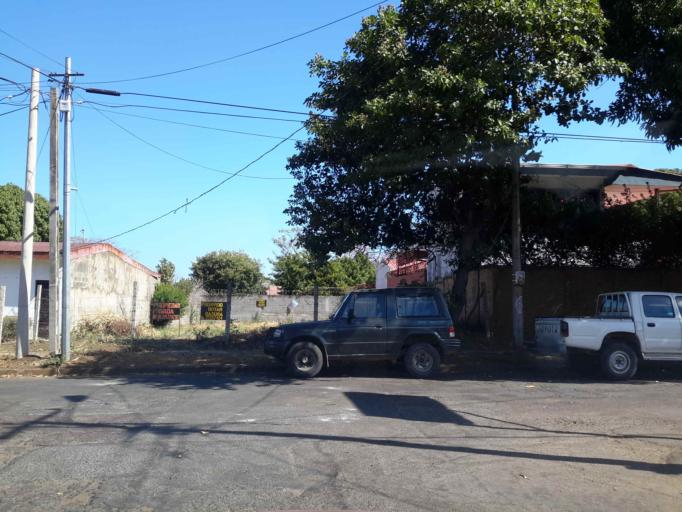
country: NI
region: Managua
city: Managua
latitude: 12.1231
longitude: -86.2710
